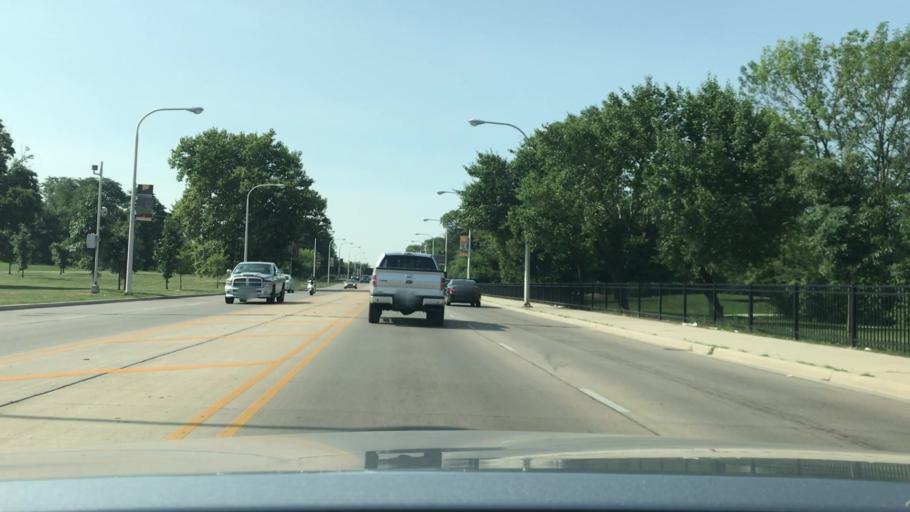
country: US
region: Illinois
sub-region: Cook County
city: Hometown
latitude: 41.7683
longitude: -87.7029
